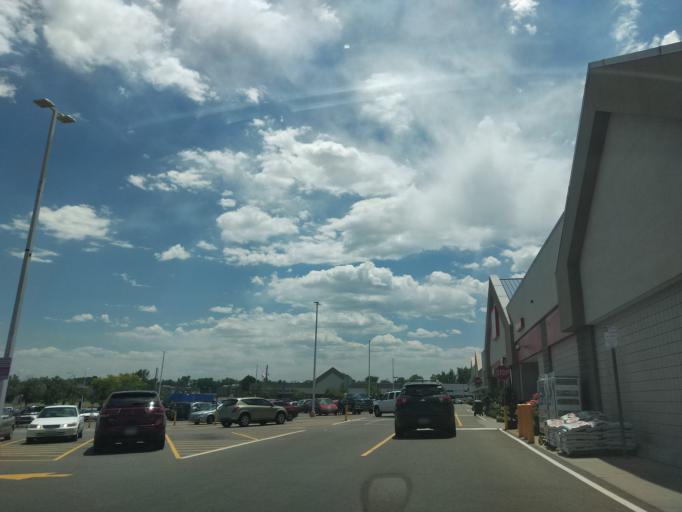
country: US
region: Colorado
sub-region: Jefferson County
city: Lakewood
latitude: 39.6819
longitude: -105.0829
